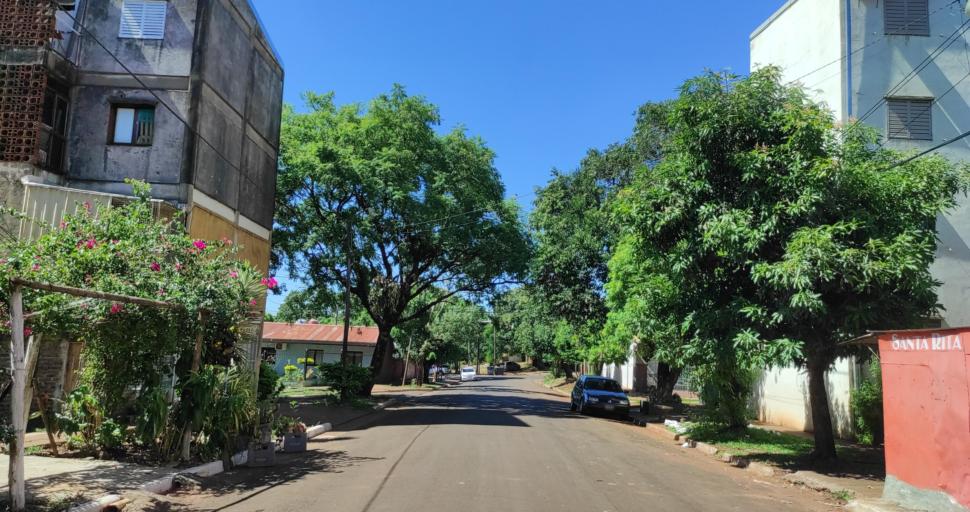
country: AR
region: Misiones
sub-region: Departamento de Capital
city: Posadas
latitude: -27.3729
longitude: -55.9504
